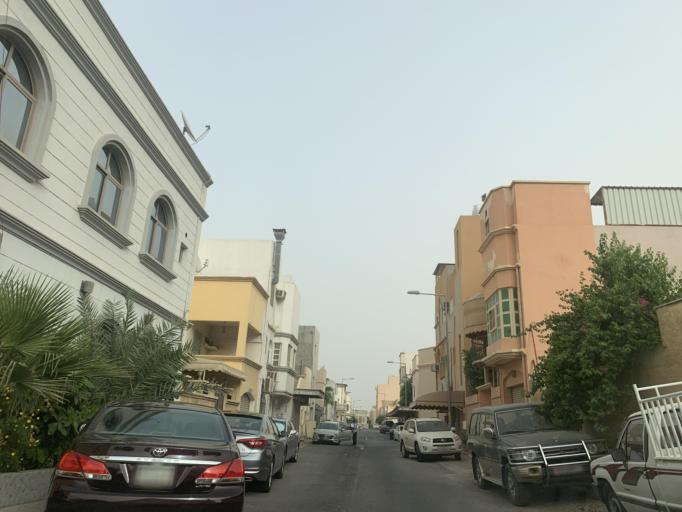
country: BH
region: Northern
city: Madinat `Isa
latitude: 26.1639
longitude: 50.5653
